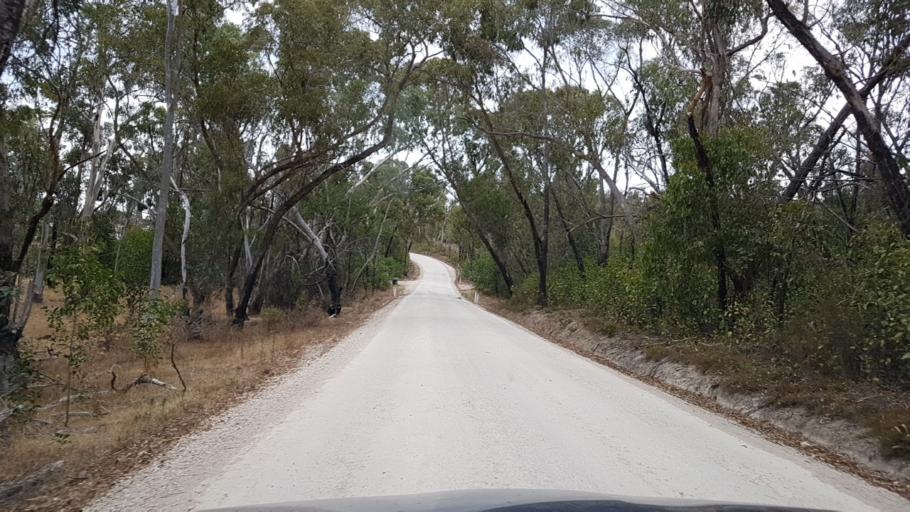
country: AU
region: South Australia
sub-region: Adelaide Hills
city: Gumeracha
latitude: -34.7924
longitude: 138.8350
